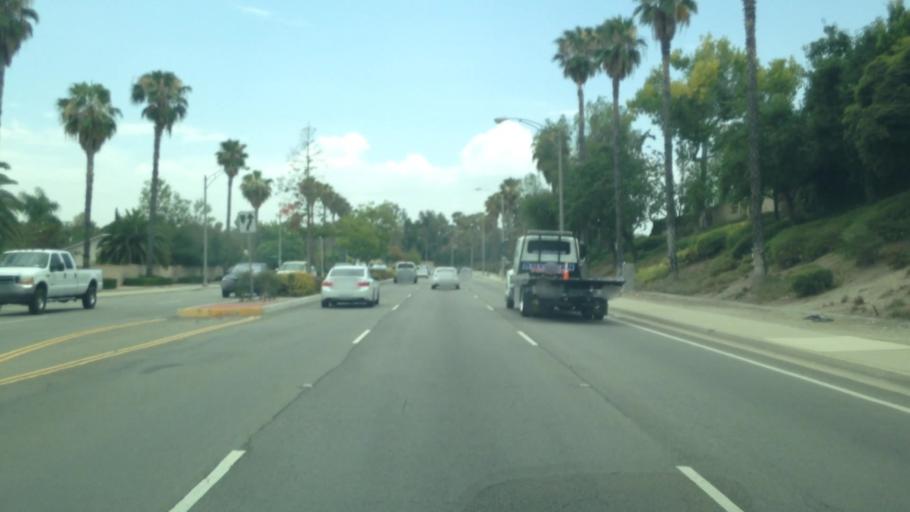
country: US
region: California
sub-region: Riverside County
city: Riverside
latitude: 33.9358
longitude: -117.3508
